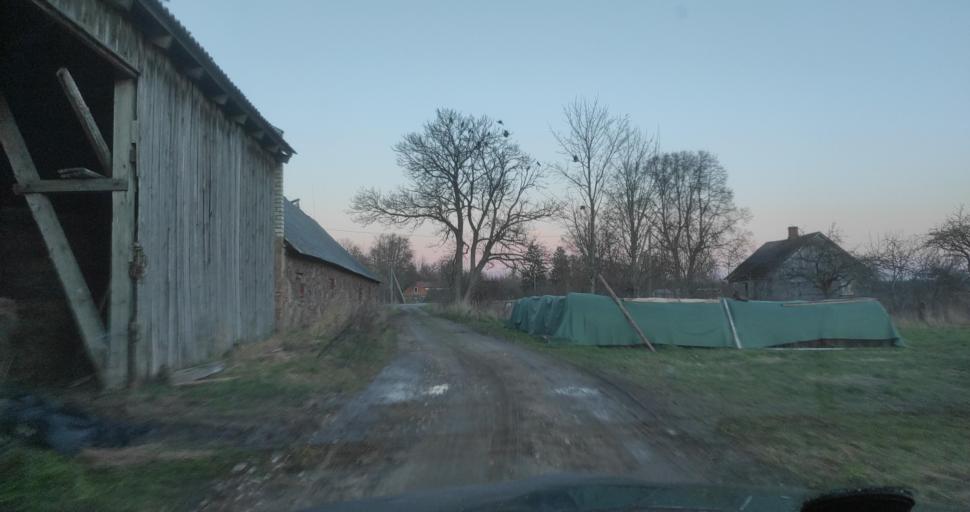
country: LV
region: Dundaga
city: Dundaga
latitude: 57.3746
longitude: 22.2285
